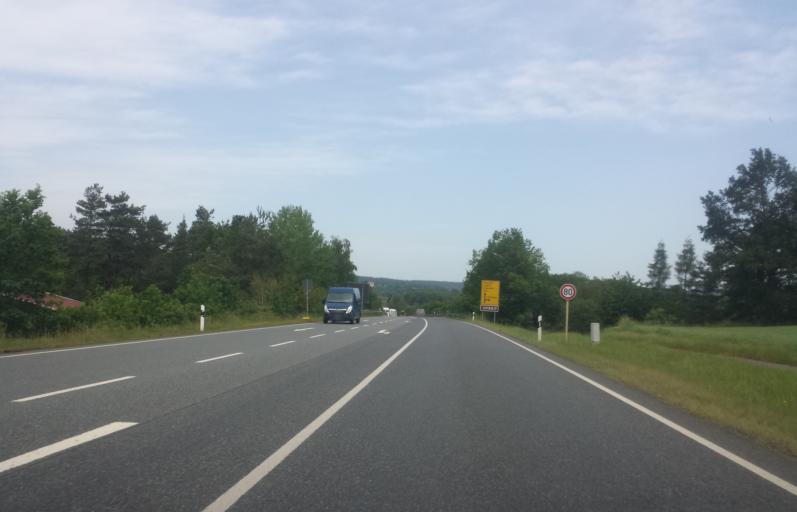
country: DE
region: Bavaria
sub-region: Upper Palatinate
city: Pressath
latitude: 49.7623
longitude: 11.9235
